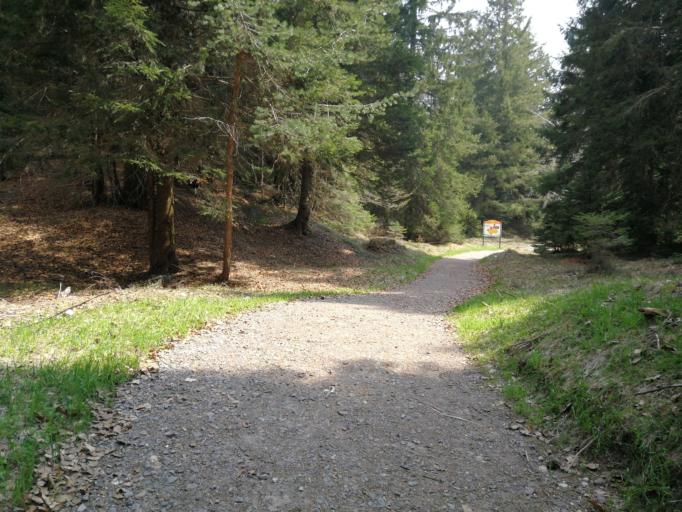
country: IT
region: Trentino-Alto Adige
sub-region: Provincia di Trento
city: Molveno
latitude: 46.1557
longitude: 10.9635
